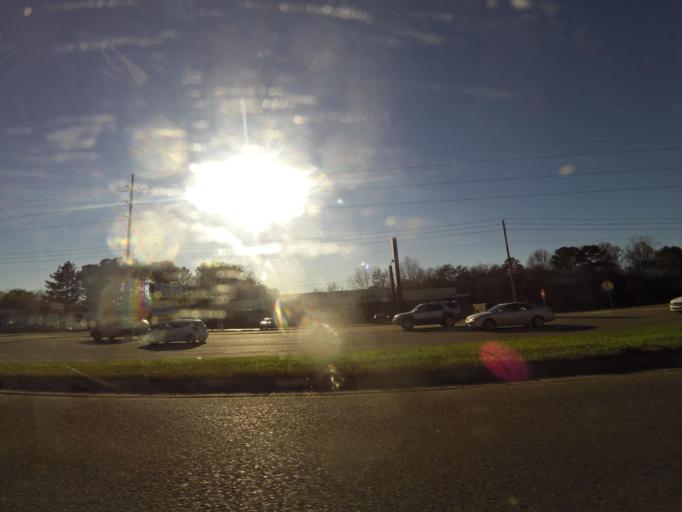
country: US
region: Alabama
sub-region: Houston County
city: Dothan
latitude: 31.2136
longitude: -85.4294
